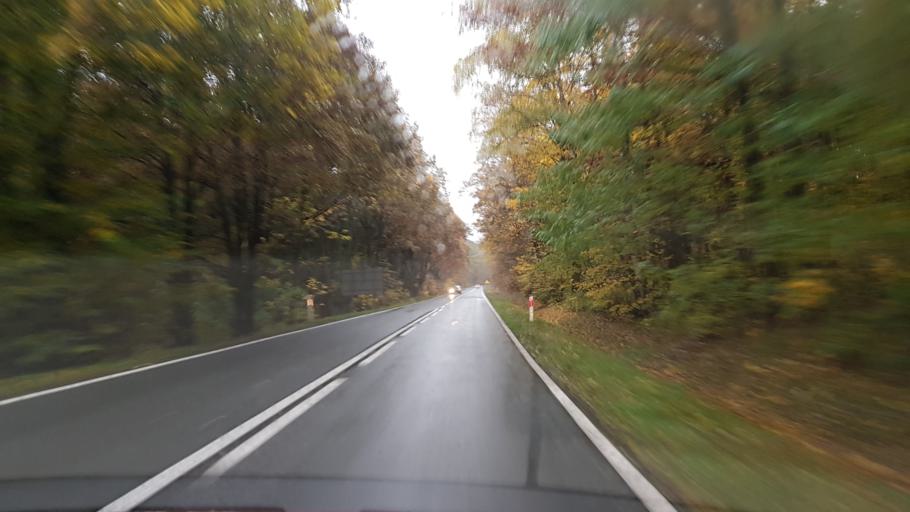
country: PL
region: West Pomeranian Voivodeship
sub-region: Powiat gryfinski
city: Chojna
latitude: 53.0416
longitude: 14.4545
